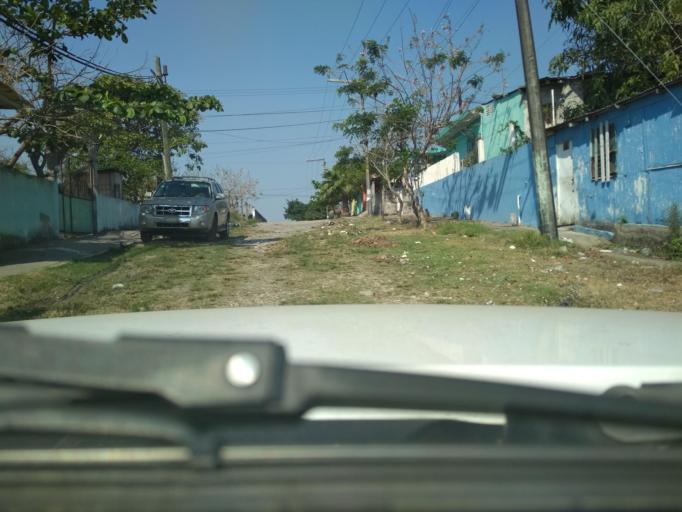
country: MX
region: Veracruz
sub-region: Veracruz
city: Colonia el Renacimiento
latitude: 19.2185
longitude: -96.2135
